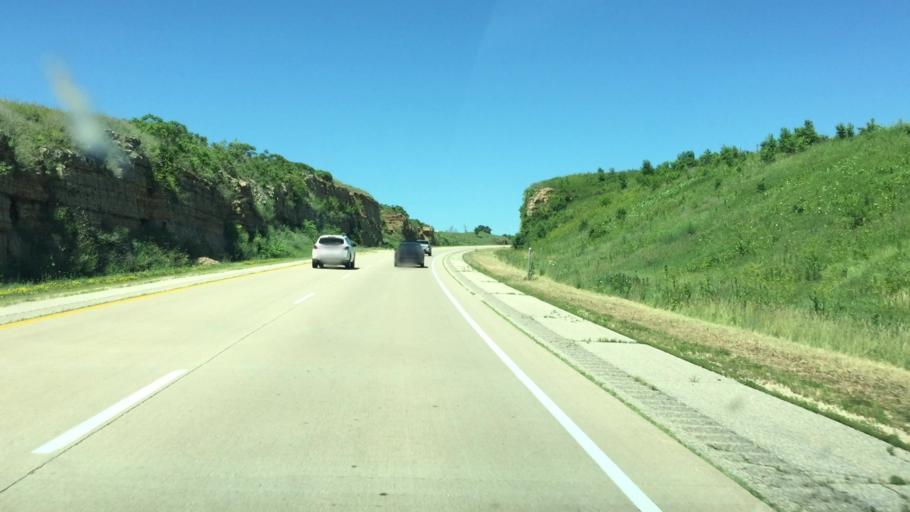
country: US
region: Wisconsin
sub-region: Iowa County
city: Mineral Point
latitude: 42.8752
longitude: -90.1910
